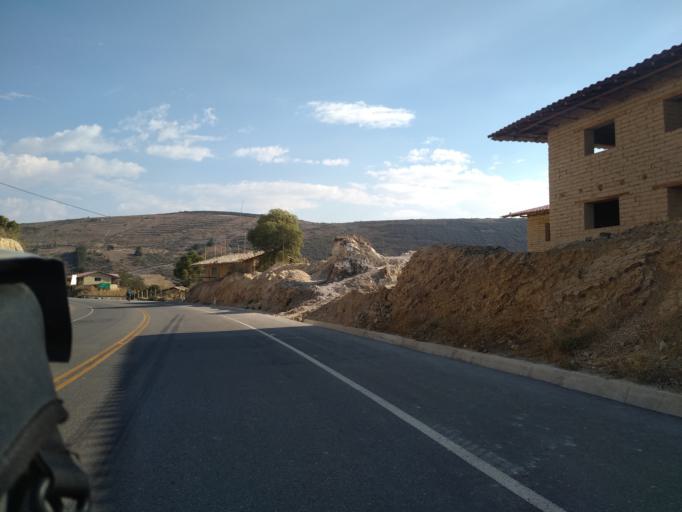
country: PE
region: Cajamarca
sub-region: San Marcos
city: San Marcos
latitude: -7.3712
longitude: -78.1290
